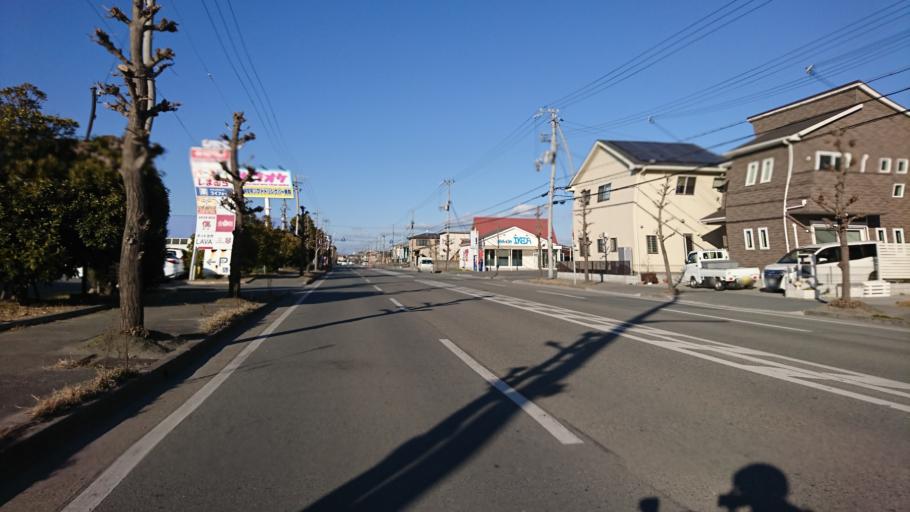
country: JP
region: Hyogo
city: Kakogawacho-honmachi
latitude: 34.7338
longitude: 134.8217
